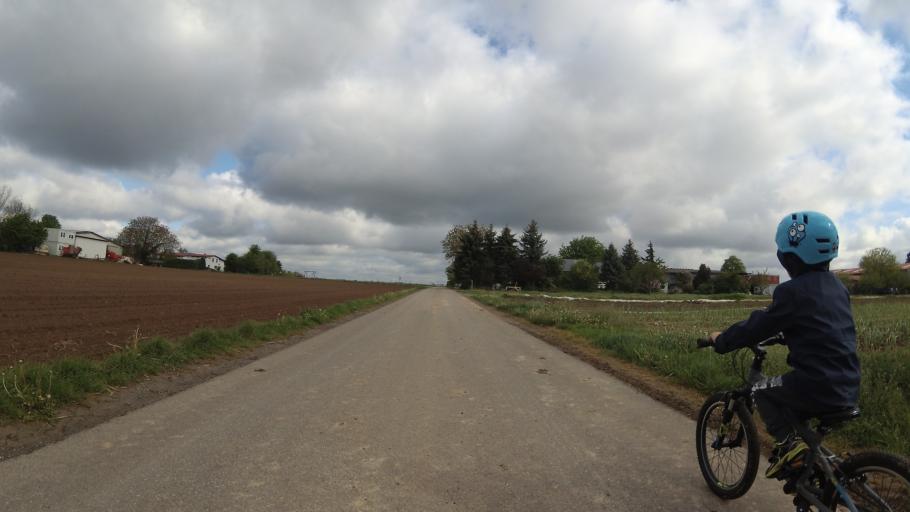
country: DE
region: Baden-Wuerttemberg
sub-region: Regierungsbezirk Stuttgart
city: Oedheim
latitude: 49.2191
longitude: 9.2409
